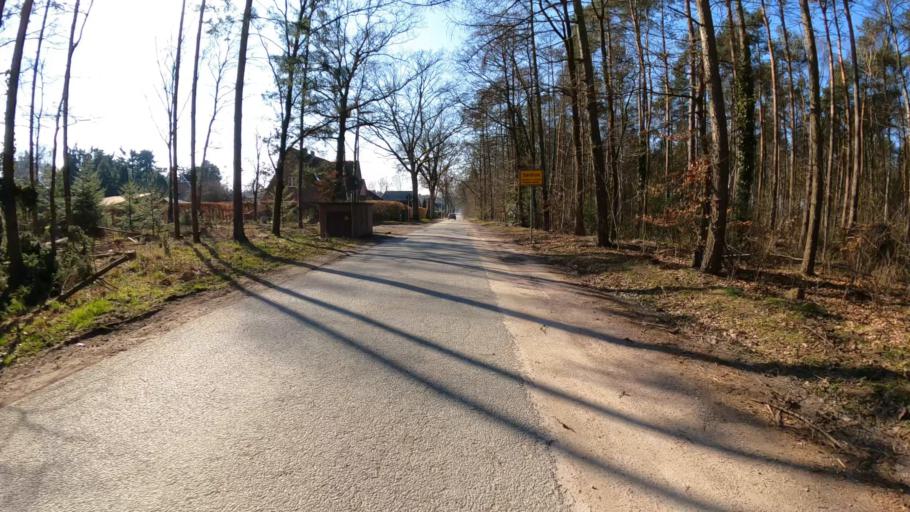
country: DE
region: Lower Saxony
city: Buchholz in der Nordheide
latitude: 53.3099
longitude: 9.8348
